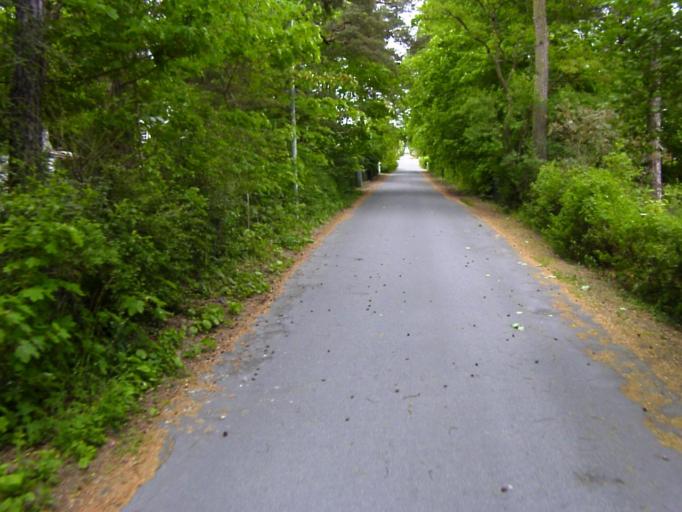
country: SE
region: Skane
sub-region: Kristianstads Kommun
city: Ahus
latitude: 55.9317
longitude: 14.3122
